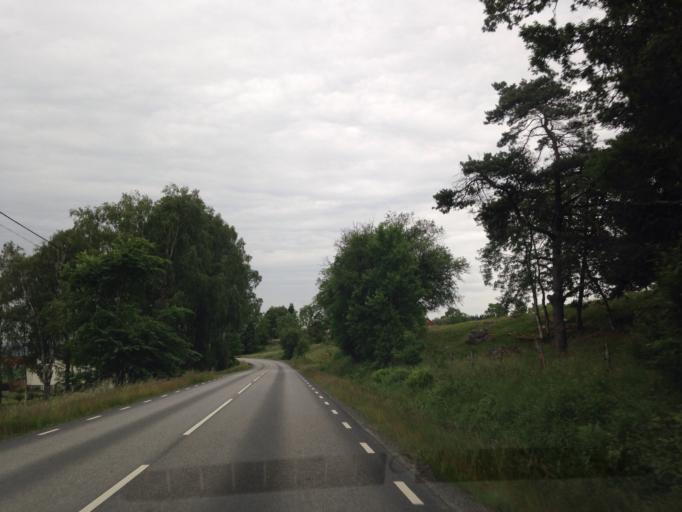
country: SE
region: Vaestra Goetaland
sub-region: Marks Kommun
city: Horred
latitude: 57.4831
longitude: 12.5210
